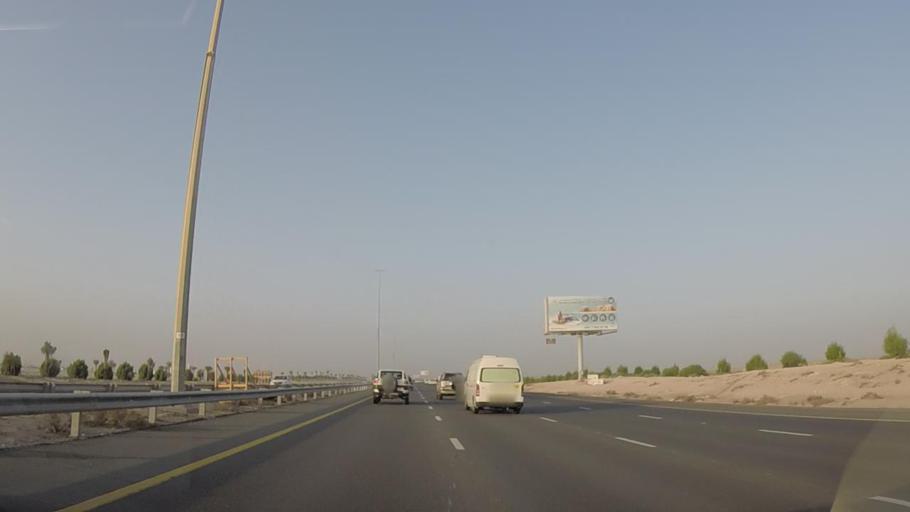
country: AE
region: Dubai
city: Dubai
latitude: 24.9106
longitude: 54.9575
